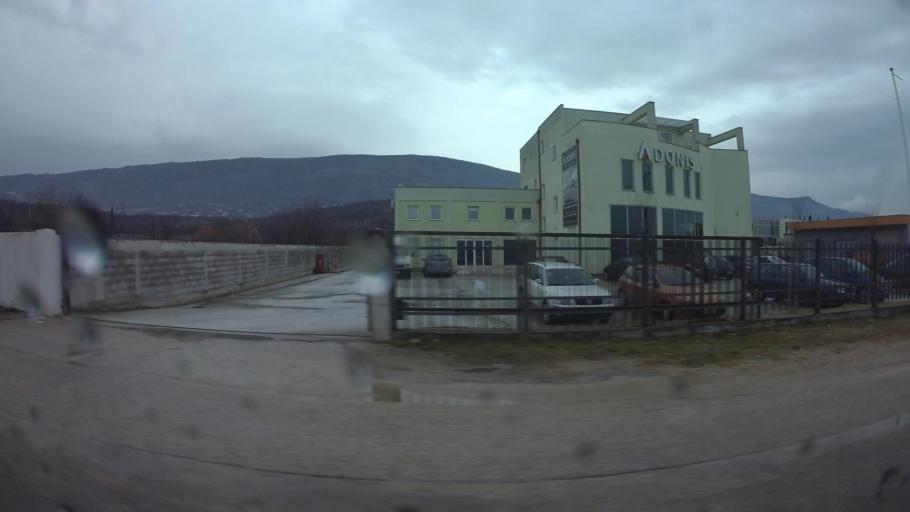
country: BA
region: Federation of Bosnia and Herzegovina
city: Rodoc
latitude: 43.2899
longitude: 17.8473
